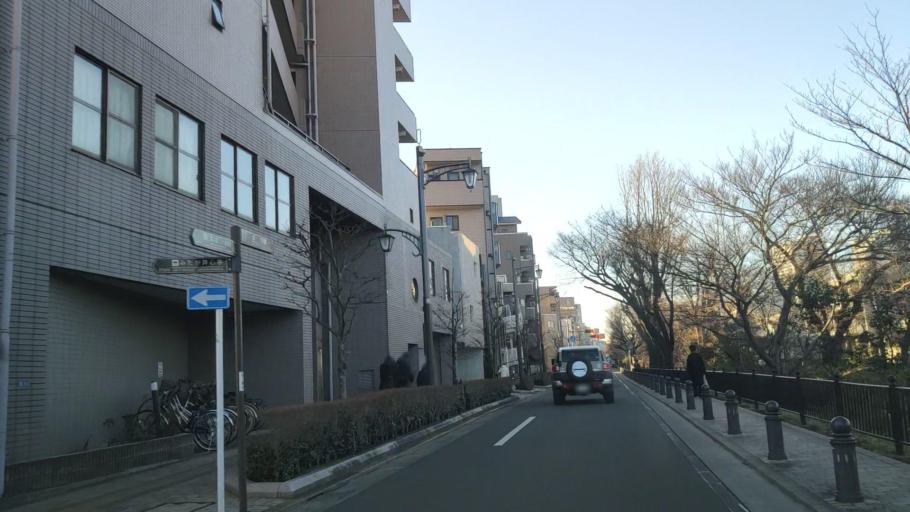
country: JP
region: Tokyo
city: Musashino
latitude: 35.7004
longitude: 139.5676
